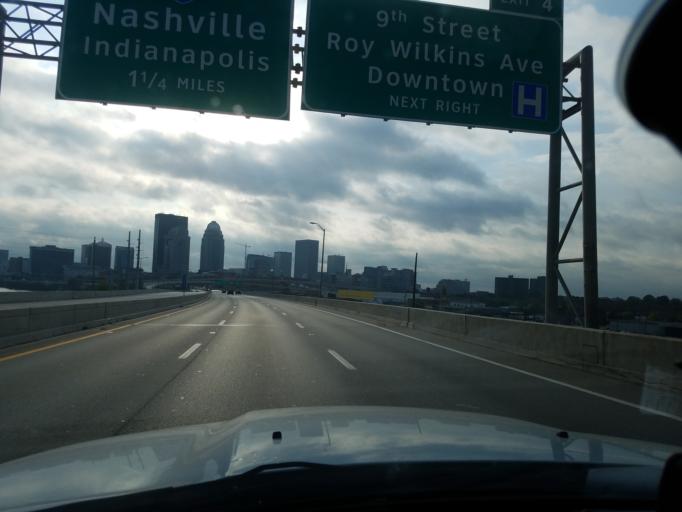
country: US
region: Kentucky
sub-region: Jefferson County
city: Louisville
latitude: 38.2614
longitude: -85.7705
